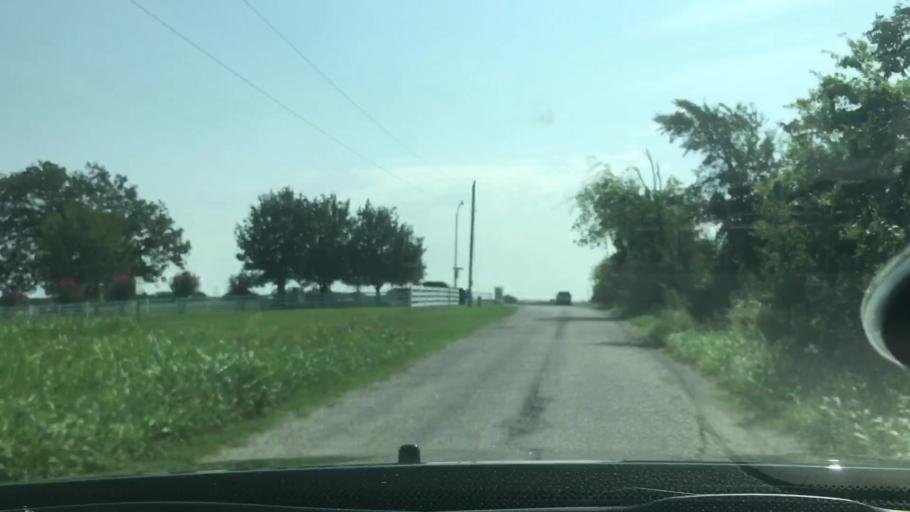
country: US
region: Oklahoma
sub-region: Bryan County
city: Durant
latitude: 34.0556
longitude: -96.3651
